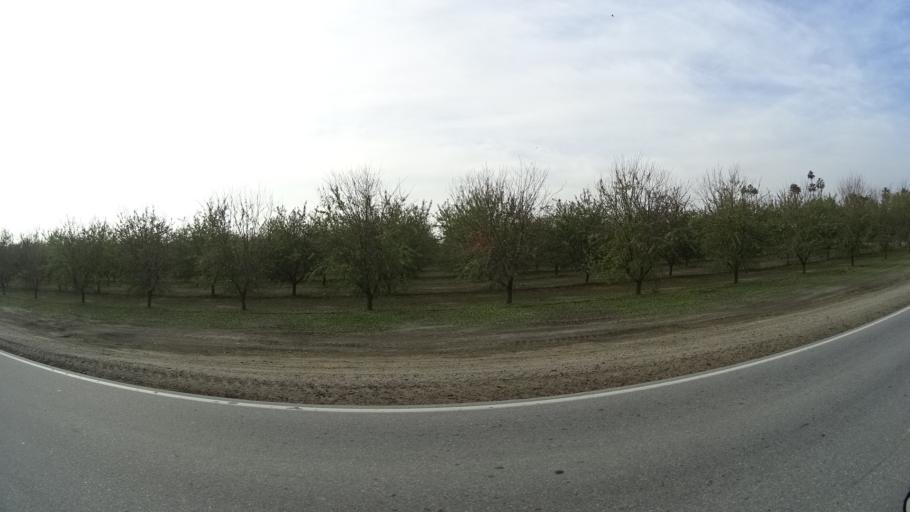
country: US
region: California
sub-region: Kern County
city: Greenacres
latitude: 35.2774
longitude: -119.1283
